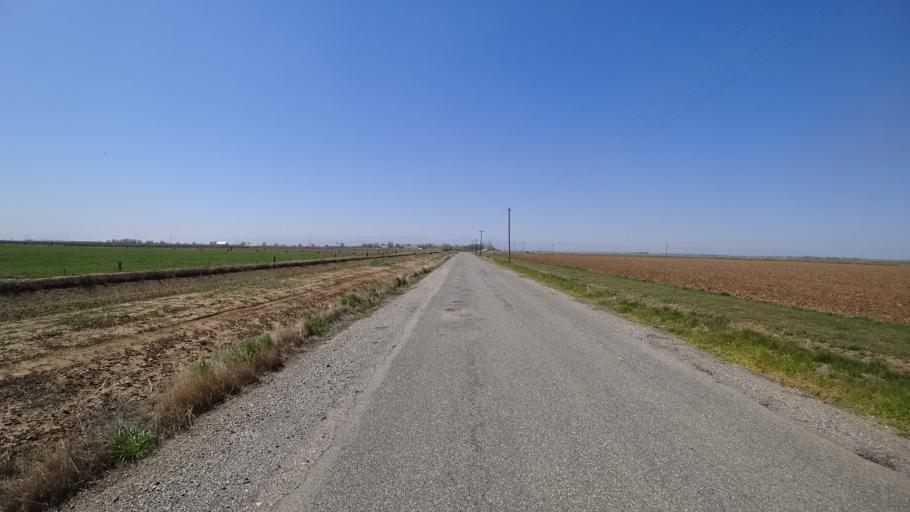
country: US
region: California
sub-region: Glenn County
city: Willows
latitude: 39.4940
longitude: -122.1330
